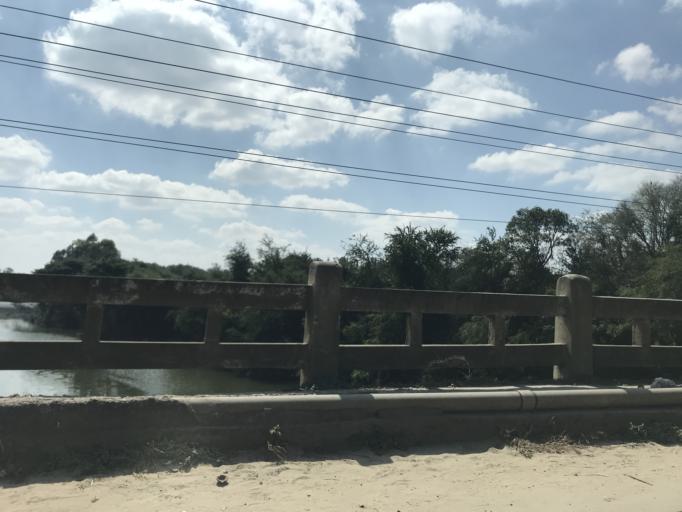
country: IN
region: Karnataka
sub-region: Mysore
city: Hunsur
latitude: 12.3131
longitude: 76.2861
